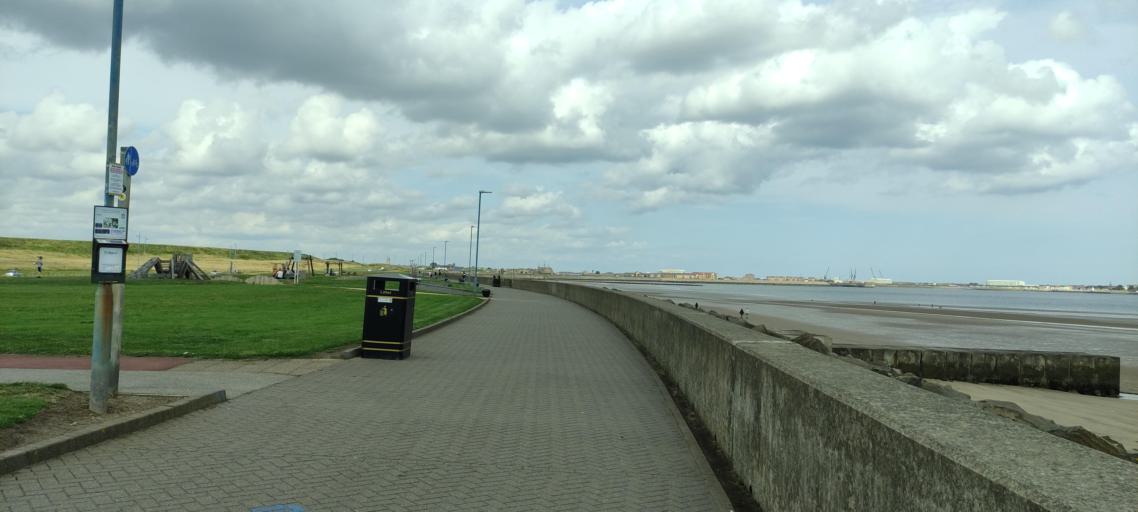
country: GB
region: England
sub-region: Hartlepool
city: Hartlepool
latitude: 54.6702
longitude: -1.1909
